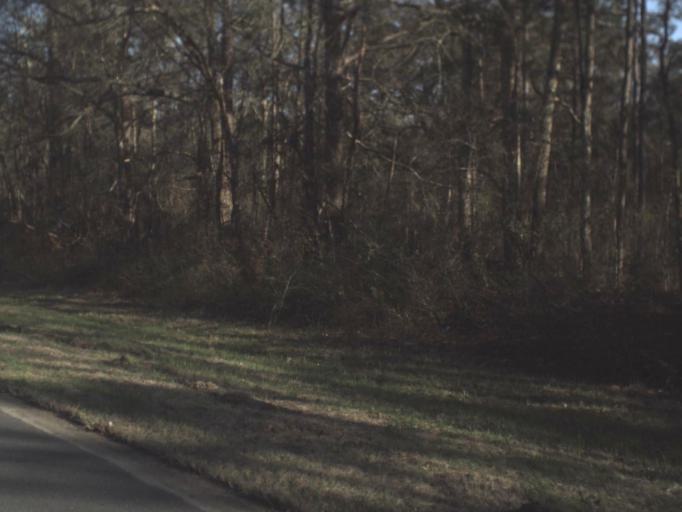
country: US
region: Florida
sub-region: Jackson County
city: Sneads
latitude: 30.7187
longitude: -84.9816
